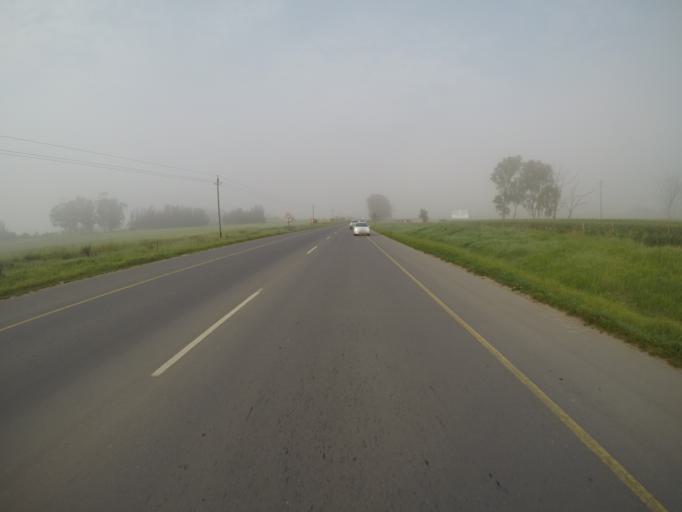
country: ZA
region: Western Cape
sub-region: City of Cape Town
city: Kraaifontein
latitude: -33.7857
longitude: 18.7025
